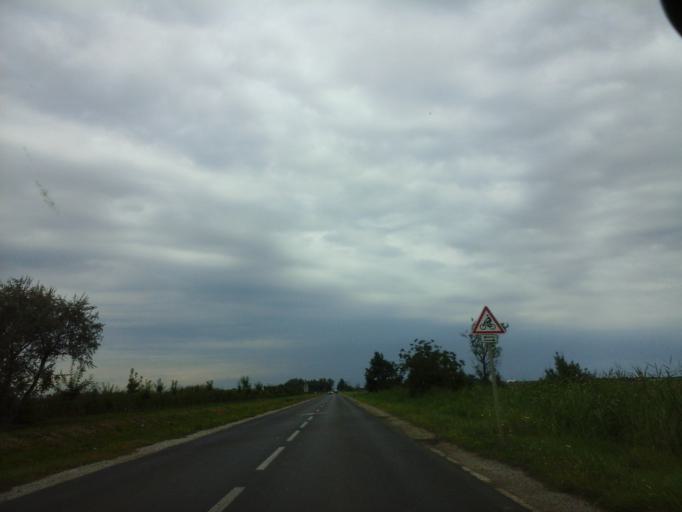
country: HU
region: Hajdu-Bihar
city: Balmazujvaros
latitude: 47.5840
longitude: 21.3473
